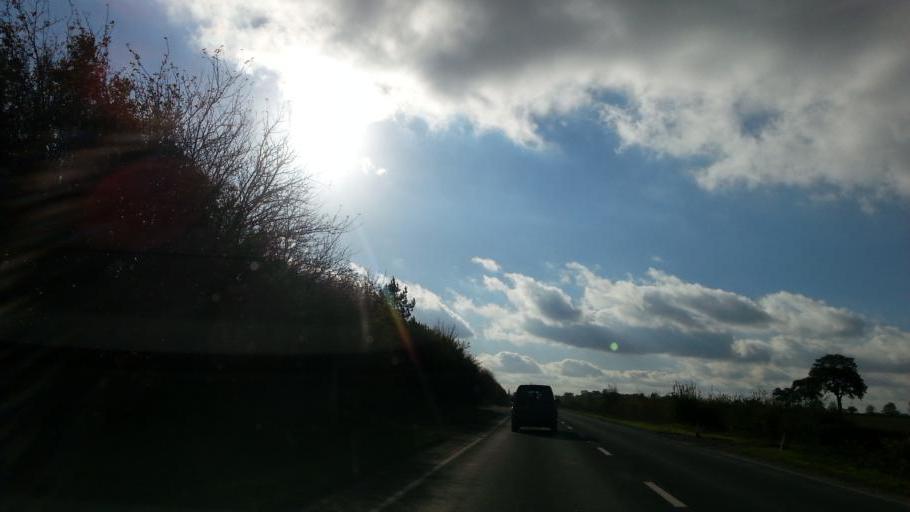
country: GB
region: England
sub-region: Norfolk
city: Harleston
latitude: 52.3845
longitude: 1.2629
